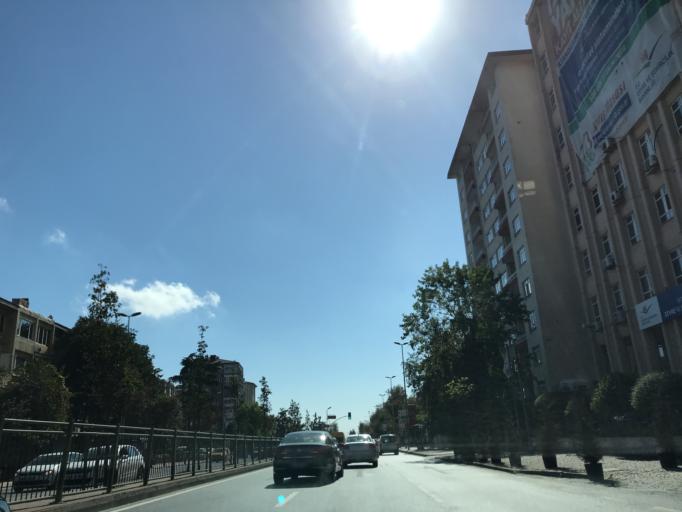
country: TR
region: Istanbul
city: Sisli
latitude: 41.0586
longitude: 29.0103
